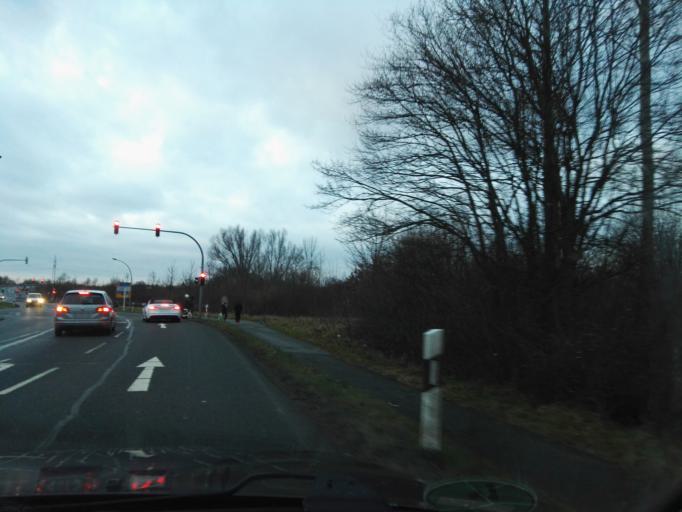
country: DE
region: Lower Saxony
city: Leiferde
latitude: 52.1963
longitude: 10.4598
